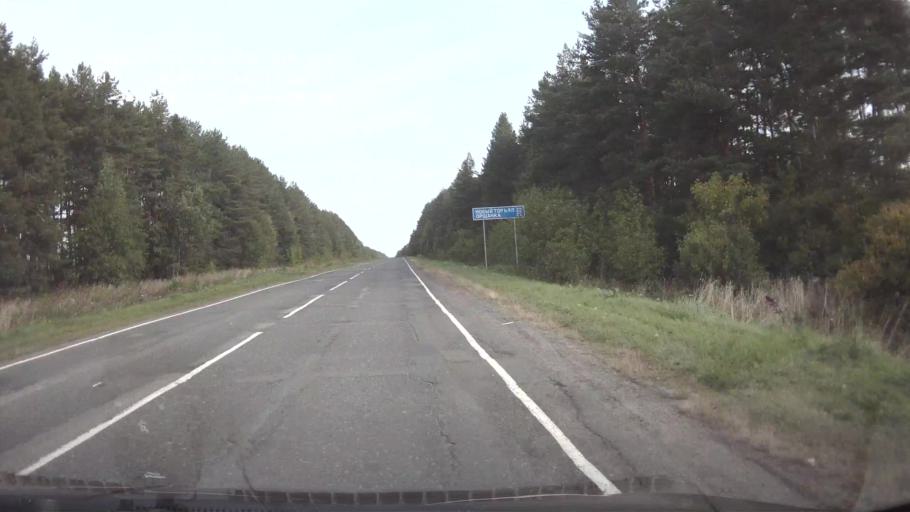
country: RU
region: Mariy-El
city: Kuzhener
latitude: 56.8190
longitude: 48.7161
